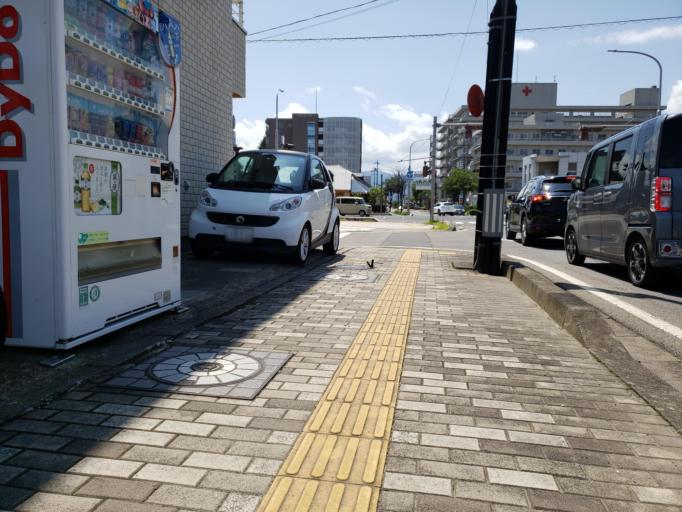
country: JP
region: Nagano
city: Nagano-shi
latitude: 36.6291
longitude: 138.1909
